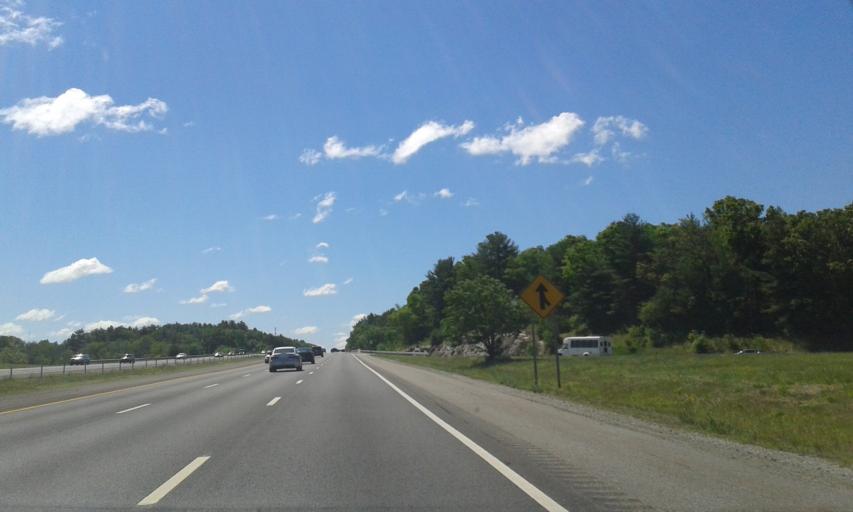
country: US
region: Massachusetts
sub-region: Middlesex County
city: Pinehurst
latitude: 42.5051
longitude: -71.2466
